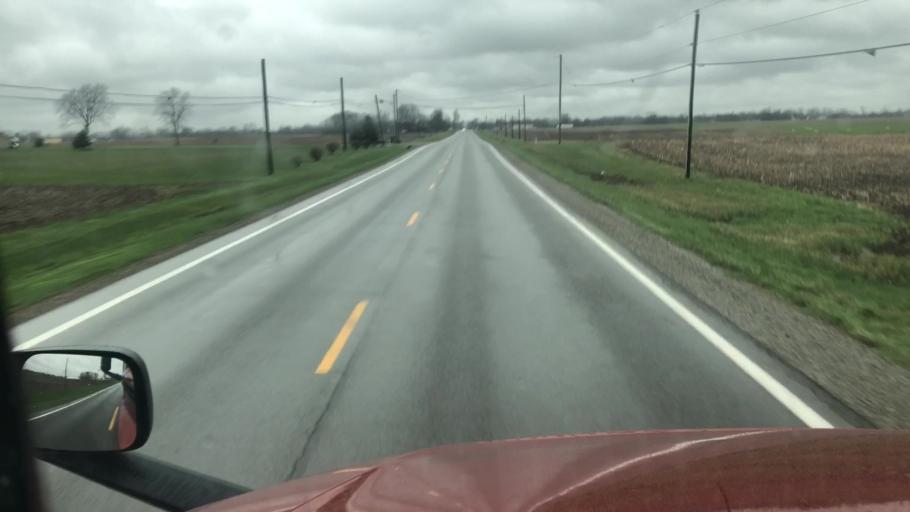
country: US
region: Ohio
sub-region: Hardin County
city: Kenton
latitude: 40.5198
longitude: -83.5097
